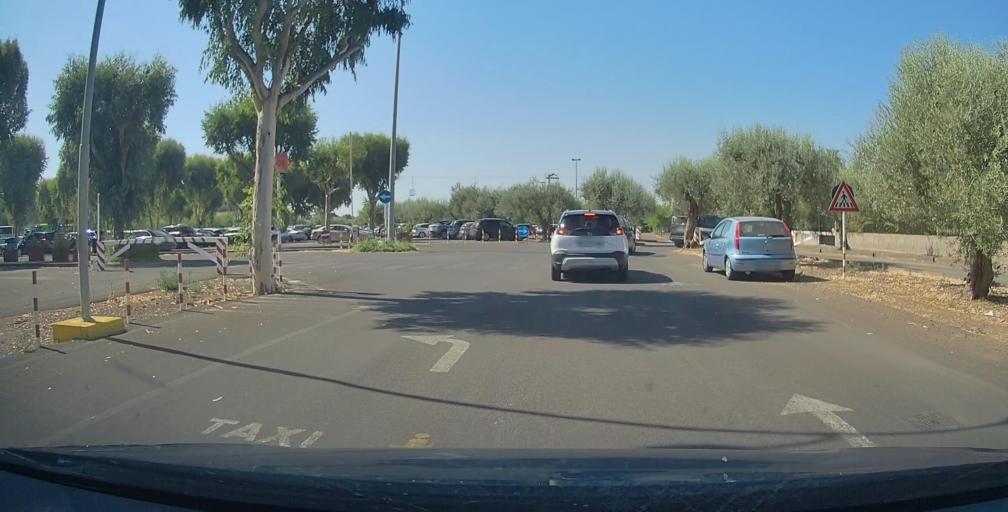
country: IT
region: Sicily
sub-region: Catania
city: Palazzolo
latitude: 37.5378
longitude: 14.9316
